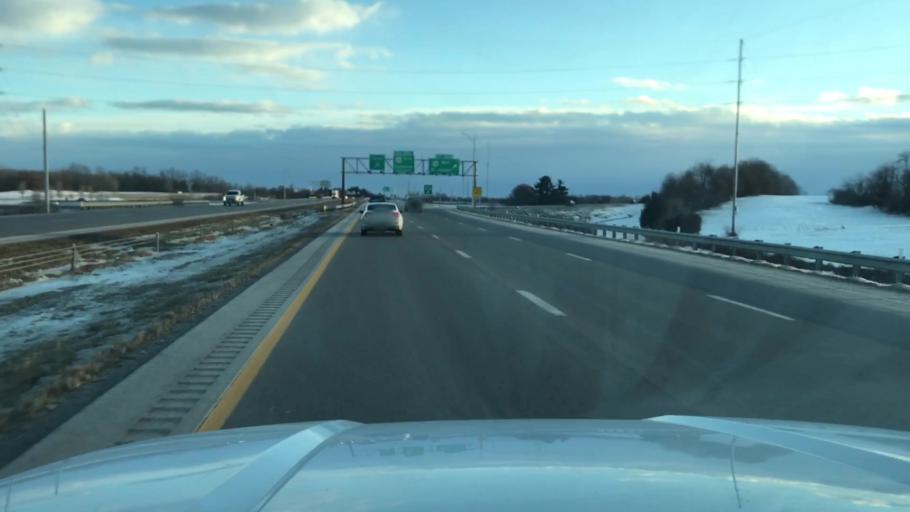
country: US
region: Missouri
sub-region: Buchanan County
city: Saint Joseph
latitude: 39.7538
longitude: -94.7903
